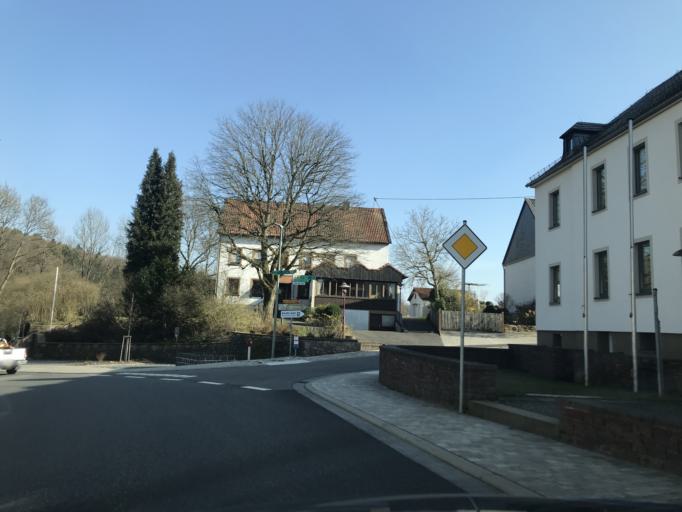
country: DE
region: Saarland
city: Nonnweiler
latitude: 49.6062
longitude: 6.9707
